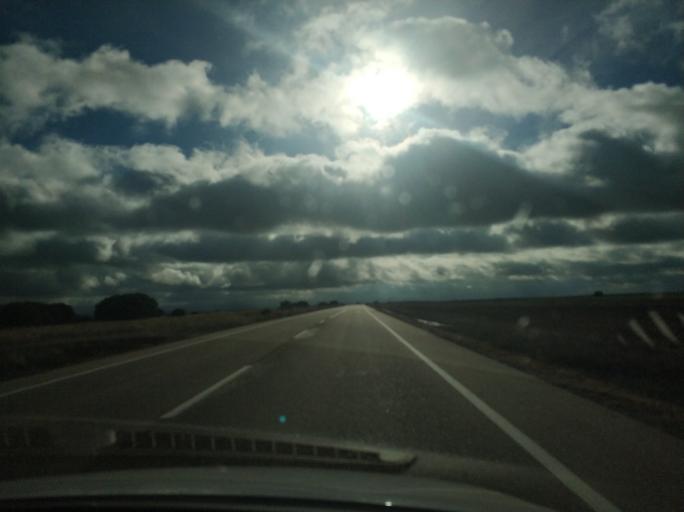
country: ES
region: Castille and Leon
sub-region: Provincia de Soria
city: Fuentecambron
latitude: 41.4896
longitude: -3.3129
